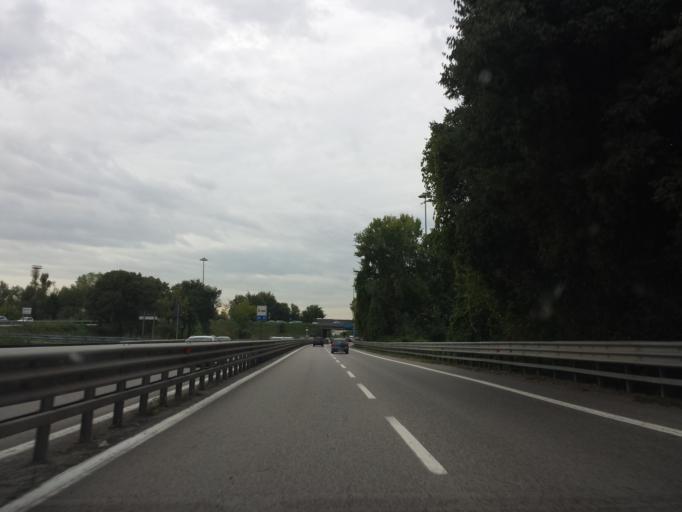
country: IT
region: Veneto
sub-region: Provincia di Padova
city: Padova
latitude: 45.4129
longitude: 11.8525
